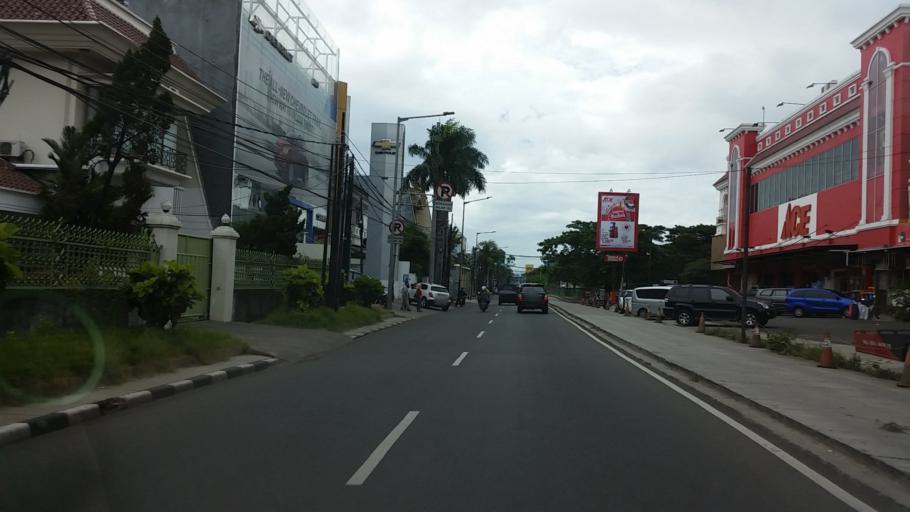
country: ID
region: Jakarta Raya
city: Jakarta
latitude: -6.1177
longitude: 106.7899
